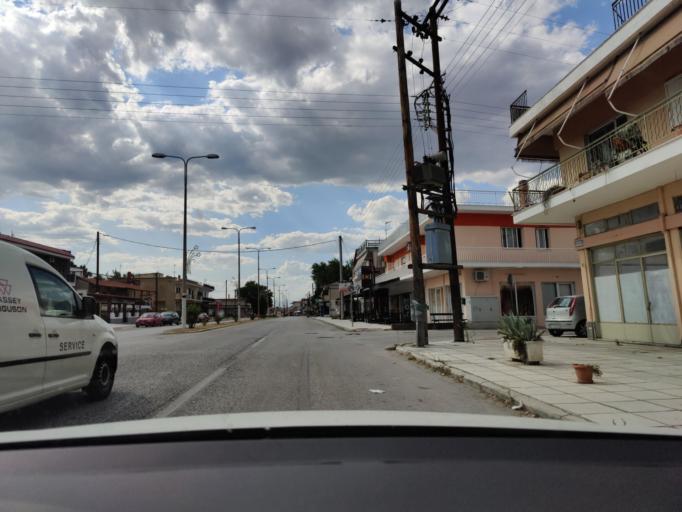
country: GR
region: Central Macedonia
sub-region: Nomos Serron
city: Lefkonas
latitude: 41.0974
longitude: 23.4992
